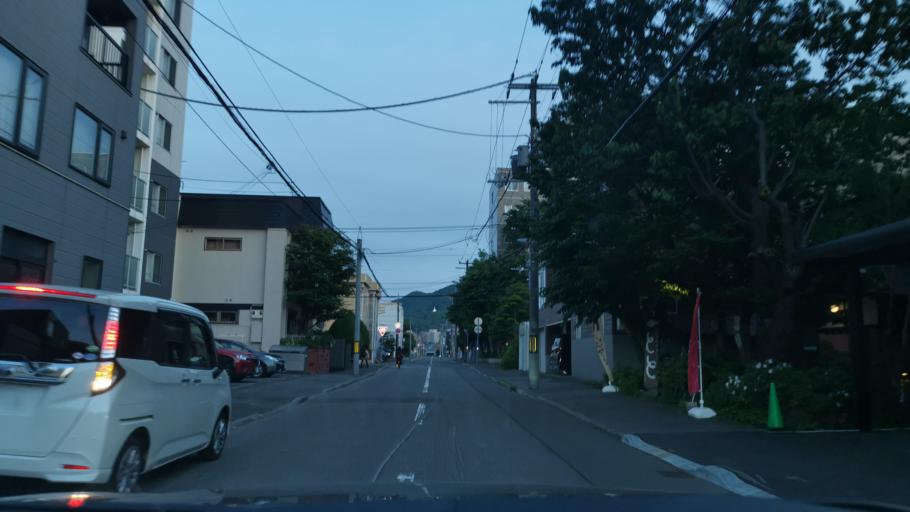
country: JP
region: Hokkaido
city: Sapporo
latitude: 43.0530
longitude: 141.3253
